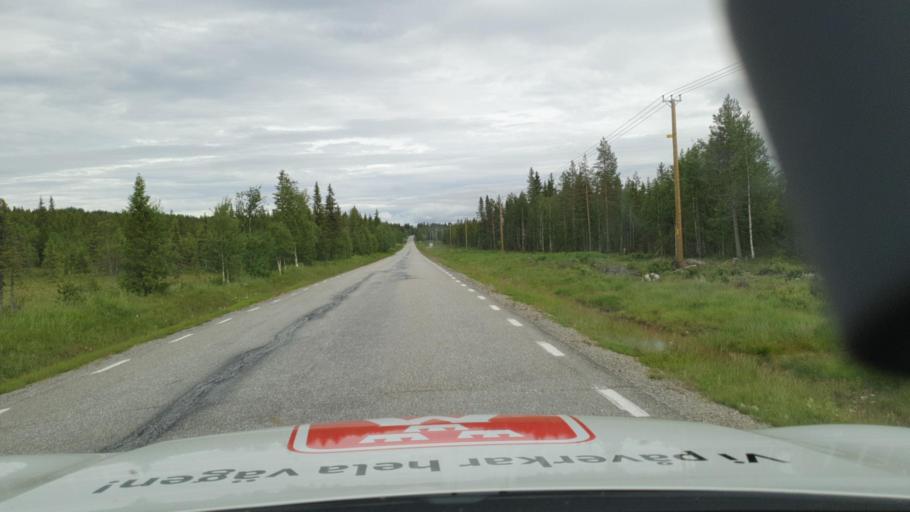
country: SE
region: Vaesterbotten
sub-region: Lycksele Kommun
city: Soderfors
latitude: 64.3666
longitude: 18.0824
